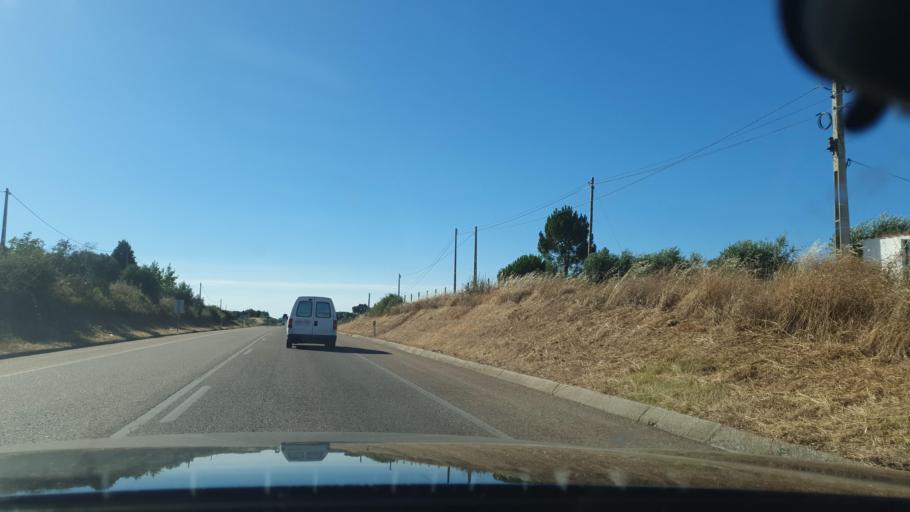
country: PT
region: Evora
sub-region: Vila Vicosa
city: Vila Vicosa
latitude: 38.7753
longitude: -7.4374
